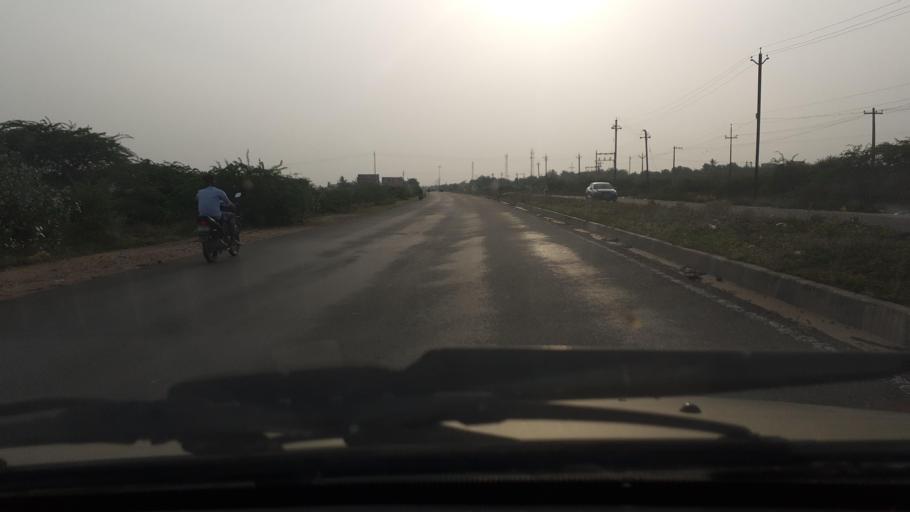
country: IN
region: Tamil Nadu
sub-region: Tirunelveli Kattabo
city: Tirunelveli
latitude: 8.7130
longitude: 77.7953
